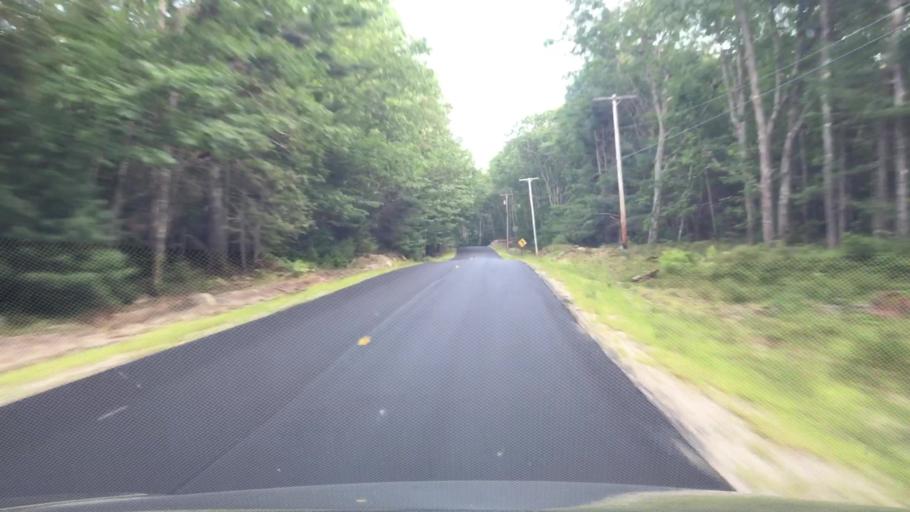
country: US
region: Maine
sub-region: Hancock County
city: Surry
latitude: 44.5216
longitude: -68.6082
